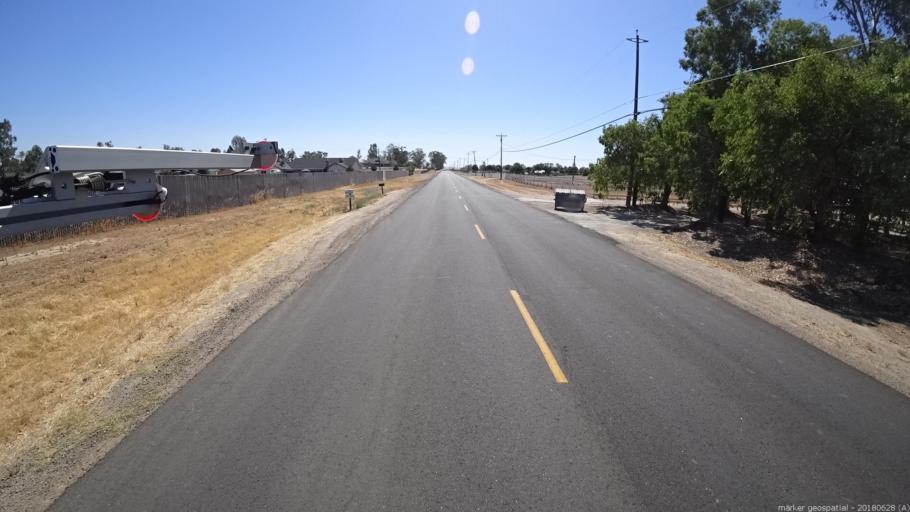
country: US
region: California
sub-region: Madera County
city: Bonadelle Ranchos-Madera Ranchos
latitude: 36.9812
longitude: -119.8884
